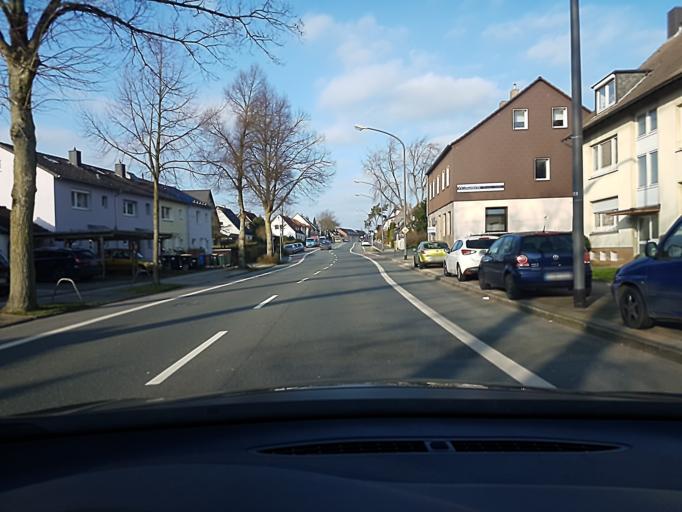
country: DE
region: North Rhine-Westphalia
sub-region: Regierungsbezirk Dusseldorf
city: Essen
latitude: 51.4215
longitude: 7.0886
